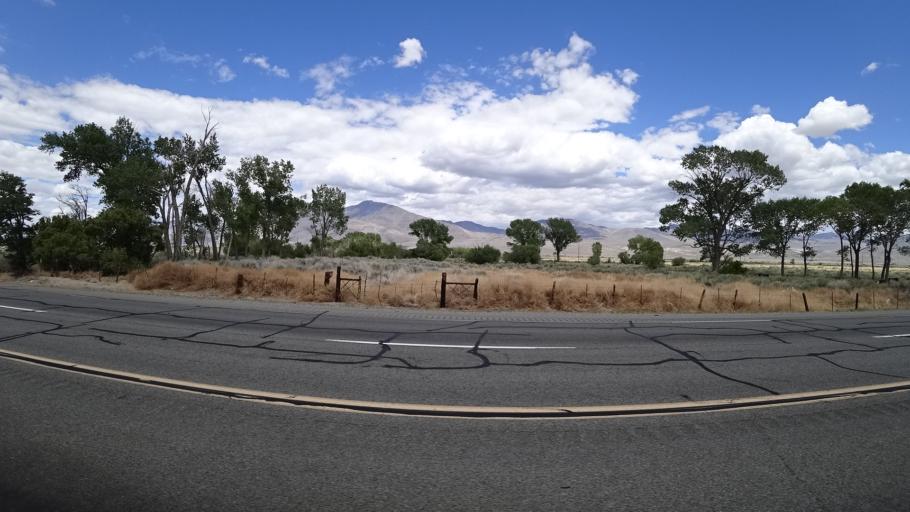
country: US
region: California
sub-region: Inyo County
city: Big Pine
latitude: 37.1844
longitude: -118.3010
